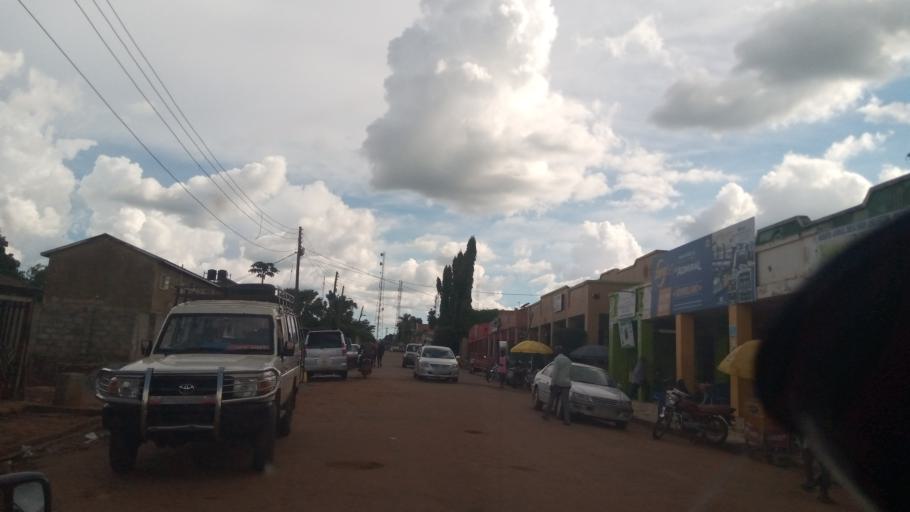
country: UG
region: Northern Region
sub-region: Lira District
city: Lira
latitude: 2.2422
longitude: 32.8976
